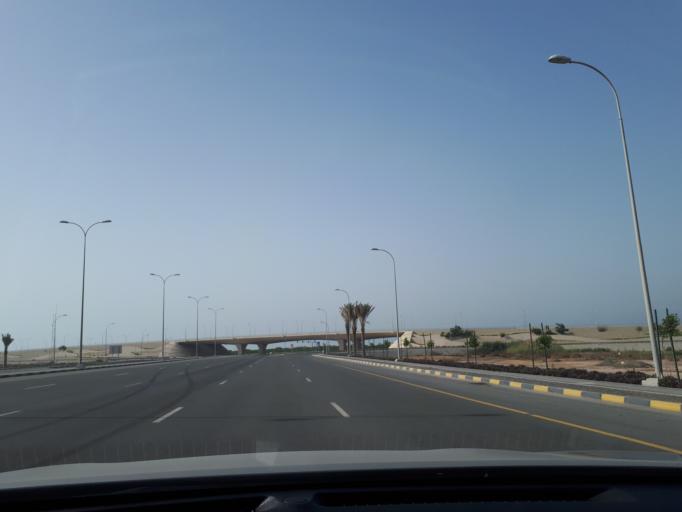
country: OM
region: Muhafazat Masqat
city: Bawshar
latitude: 23.6058
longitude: 58.3112
